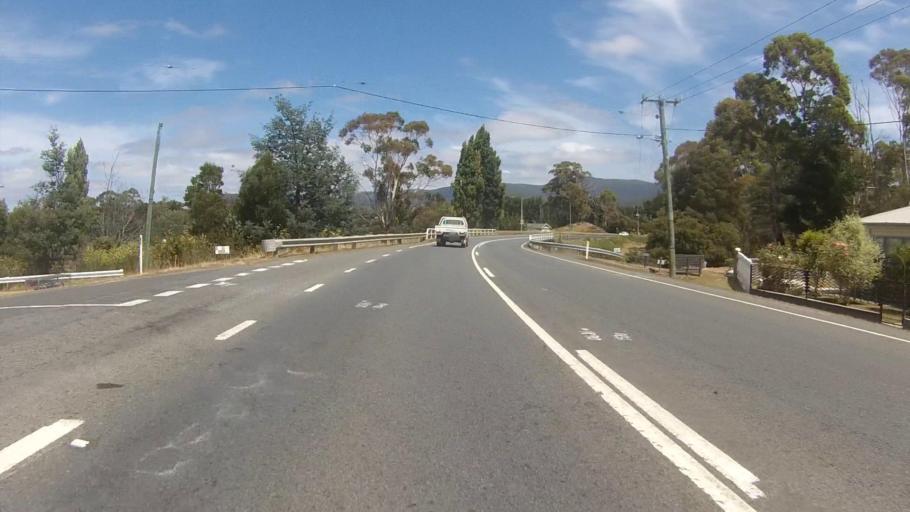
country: AU
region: Tasmania
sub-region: Kingborough
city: Margate
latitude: -43.0209
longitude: 147.2665
